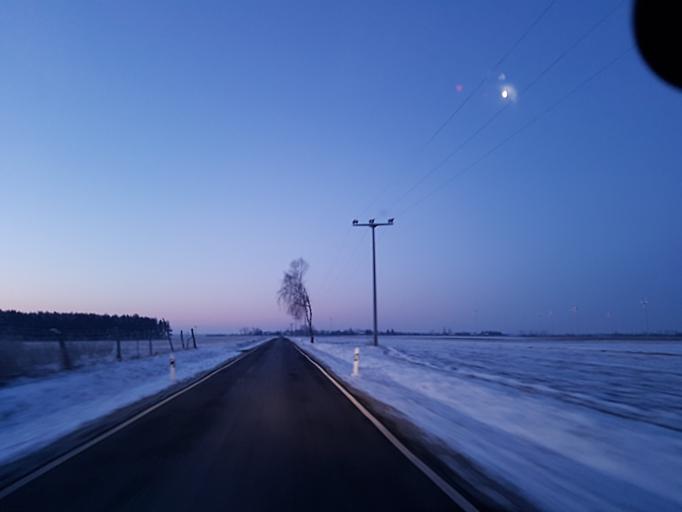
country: DE
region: Brandenburg
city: Muhlberg
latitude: 51.4865
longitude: 13.2746
